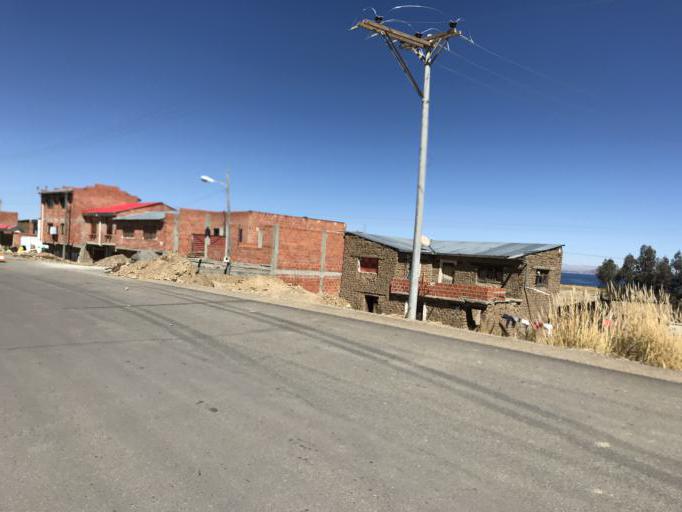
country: BO
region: La Paz
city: Huatajata
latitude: -16.2011
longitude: -68.7119
